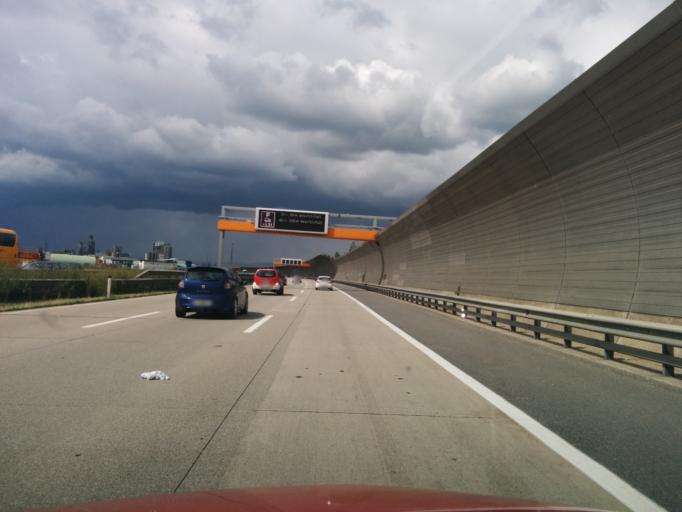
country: AT
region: Lower Austria
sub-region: Politischer Bezirk Wien-Umgebung
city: Rauchenwarth
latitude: 48.1387
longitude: 16.5250
